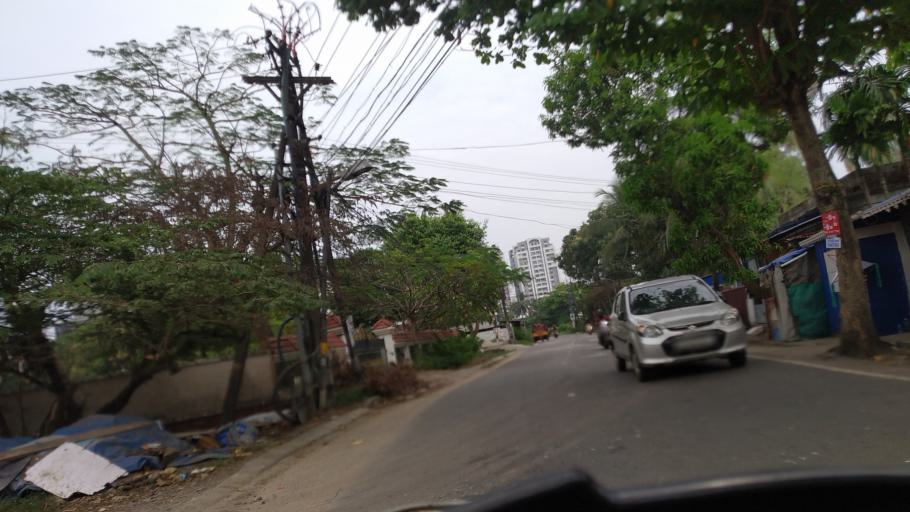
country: IN
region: Kerala
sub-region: Ernakulam
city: Cochin
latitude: 9.9531
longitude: 76.3083
